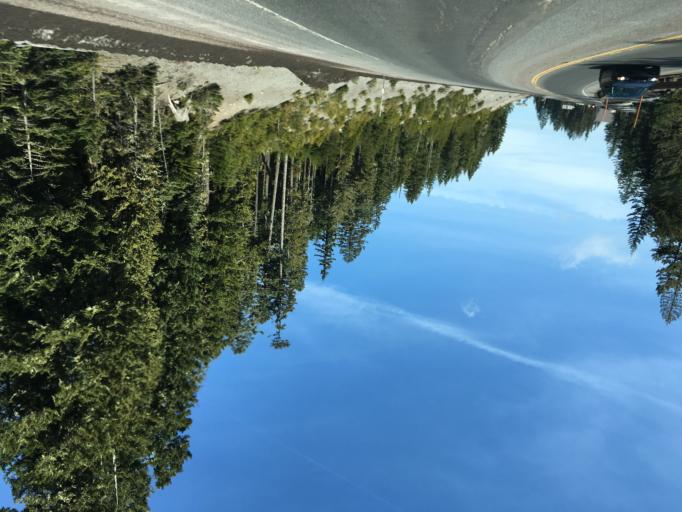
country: US
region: Oregon
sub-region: Clackamas County
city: Mount Hood Village
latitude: 45.3010
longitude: -121.7359
